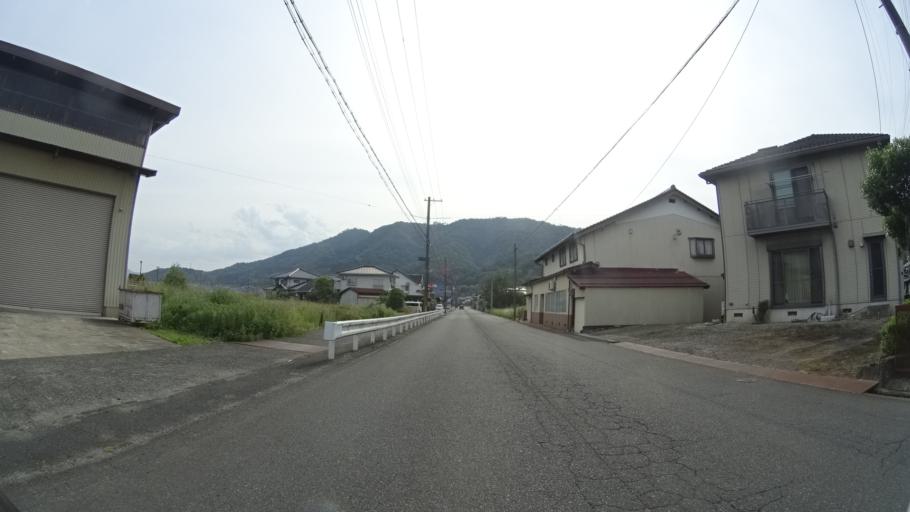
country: JP
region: Kyoto
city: Miyazu
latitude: 35.5620
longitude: 135.1473
